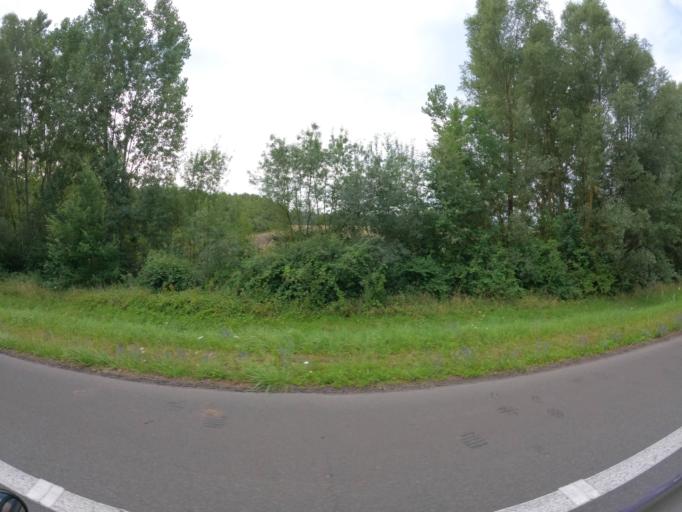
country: FR
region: Centre
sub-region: Departement d'Indre-et-Loire
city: Restigne
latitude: 47.2717
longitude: 0.2582
